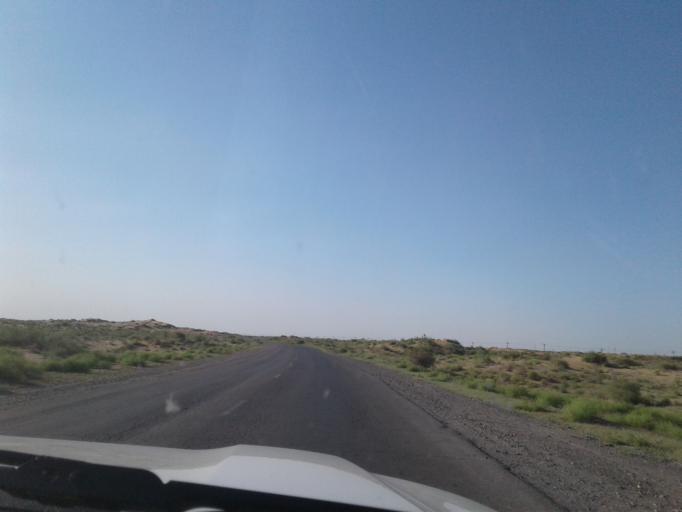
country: TM
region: Mary
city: Yoloeten
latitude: 37.1404
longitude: 62.4405
